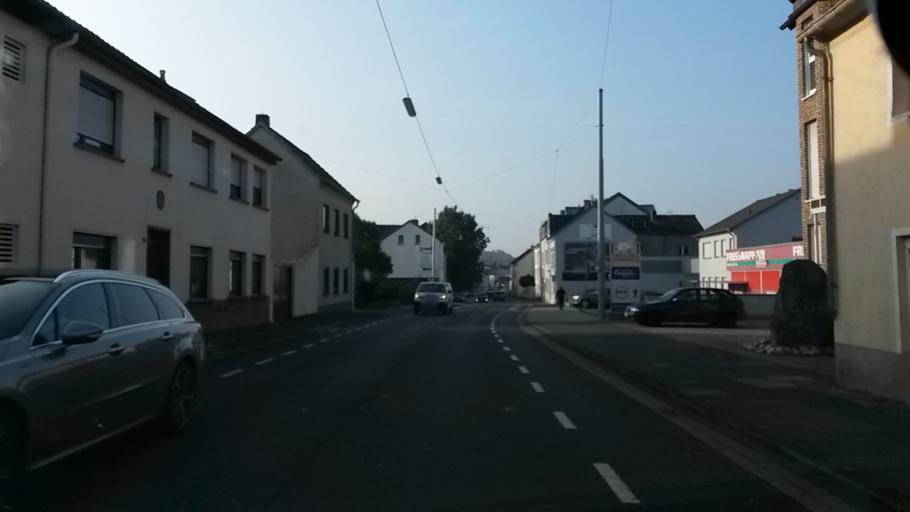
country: DE
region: North Rhine-Westphalia
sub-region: Regierungsbezirk Koln
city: Siegburg
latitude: 50.8060
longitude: 7.2089
